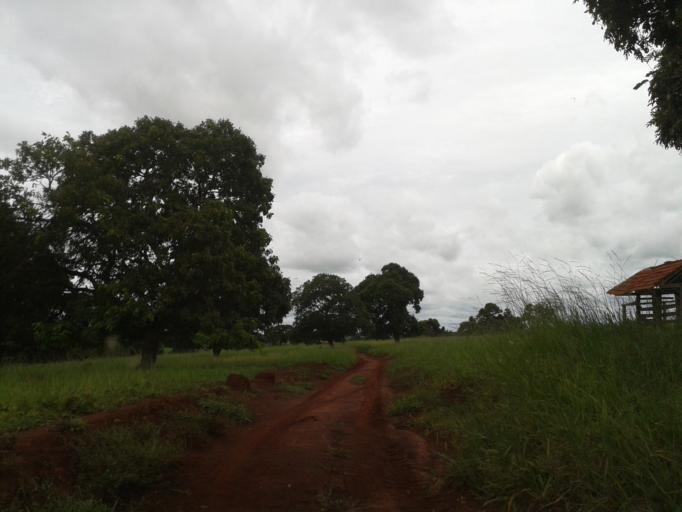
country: BR
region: Minas Gerais
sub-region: Capinopolis
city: Capinopolis
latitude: -18.7803
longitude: -49.7827
